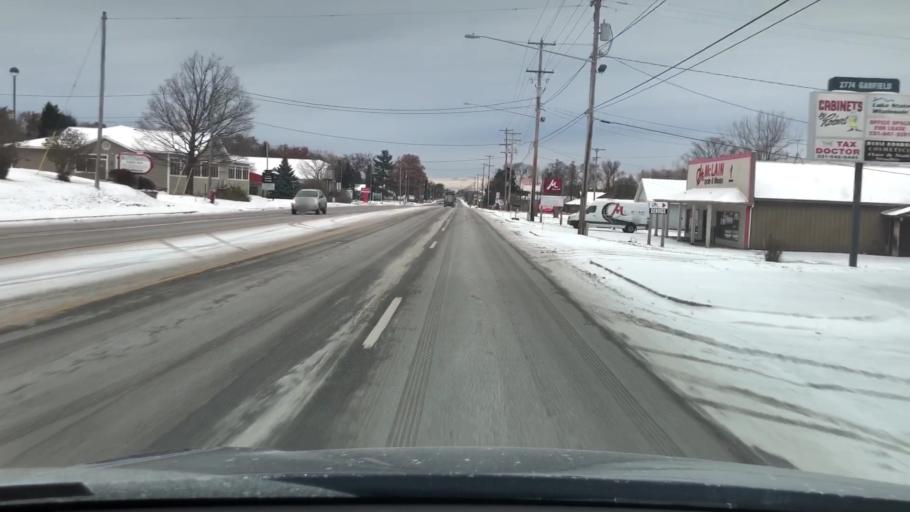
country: US
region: Michigan
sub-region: Grand Traverse County
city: Traverse City
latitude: 44.7272
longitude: -85.5953
